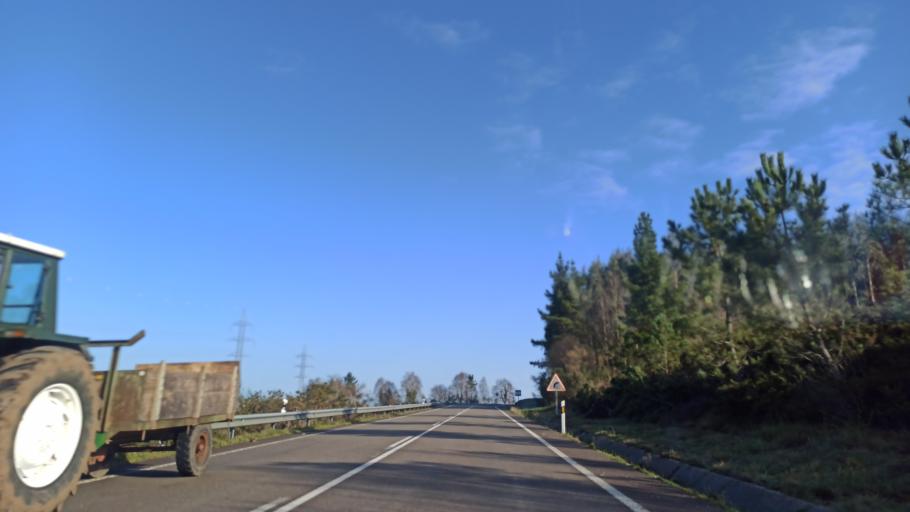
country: ES
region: Galicia
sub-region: Provincia da Coruna
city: As Pontes de Garcia Rodriguez
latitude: 43.4817
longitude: -7.8488
